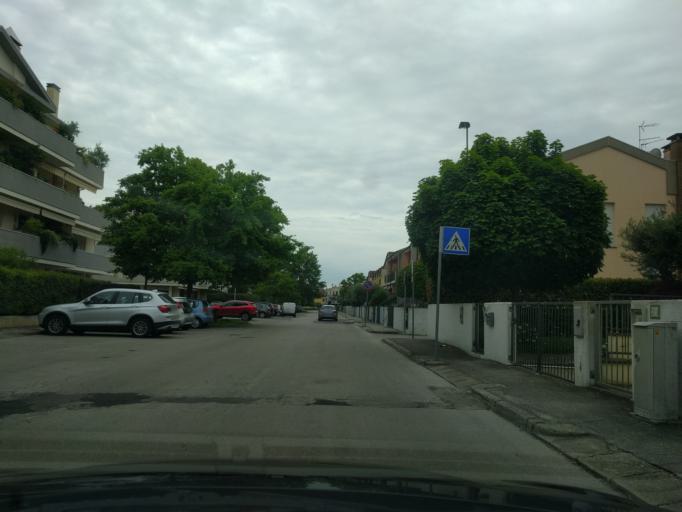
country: IT
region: Veneto
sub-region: Provincia di Rovigo
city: Rovigo
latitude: 45.0611
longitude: 11.7873
